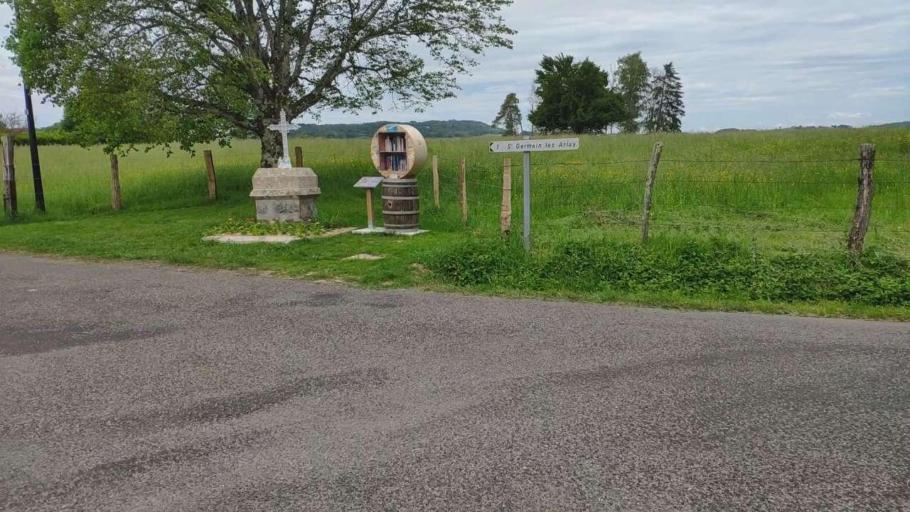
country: FR
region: Franche-Comte
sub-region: Departement du Jura
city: Perrigny
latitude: 46.7558
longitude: 5.5741
